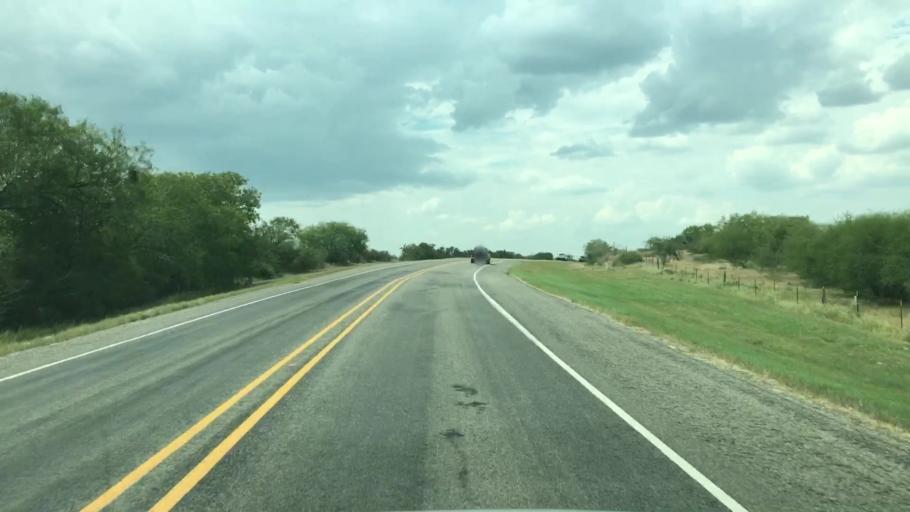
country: US
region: Texas
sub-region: Live Oak County
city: Three Rivers
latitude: 28.6406
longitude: -98.2818
